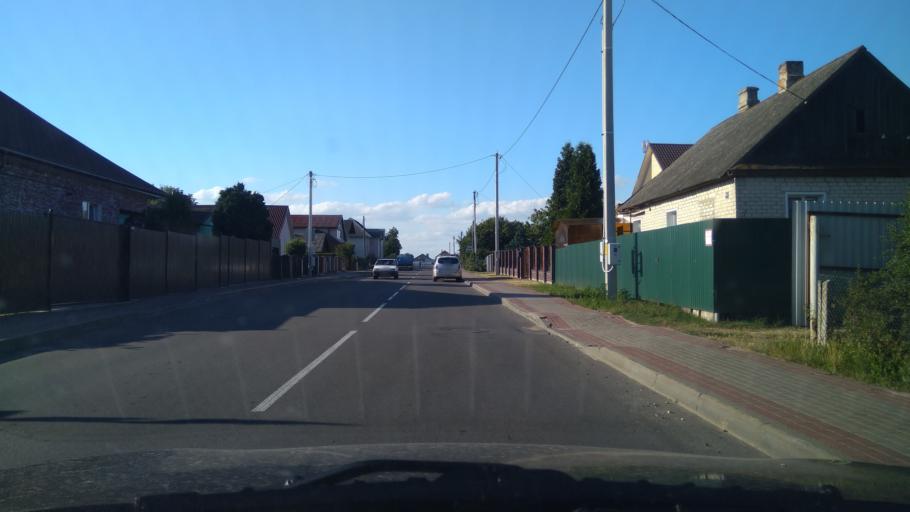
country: BY
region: Brest
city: Byaroza
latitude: 52.5384
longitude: 24.9782
